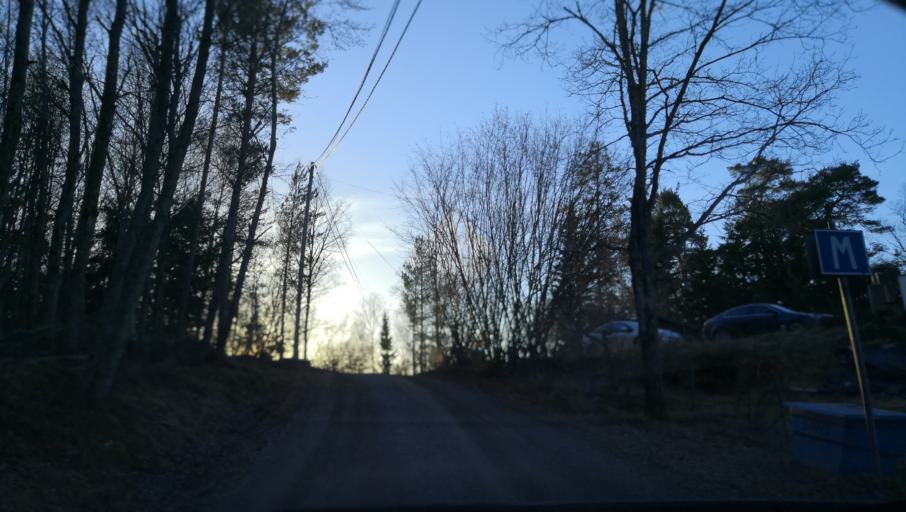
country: SE
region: Stockholm
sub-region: Varmdo Kommun
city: Mortnas
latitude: 59.3372
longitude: 18.4453
